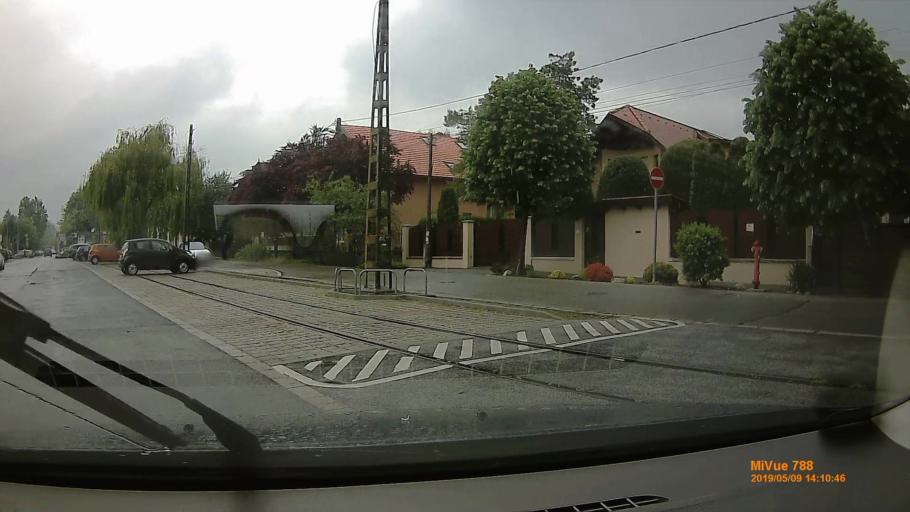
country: HU
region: Budapest
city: Budapest XVI. keruelet
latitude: 47.5093
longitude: 19.1727
